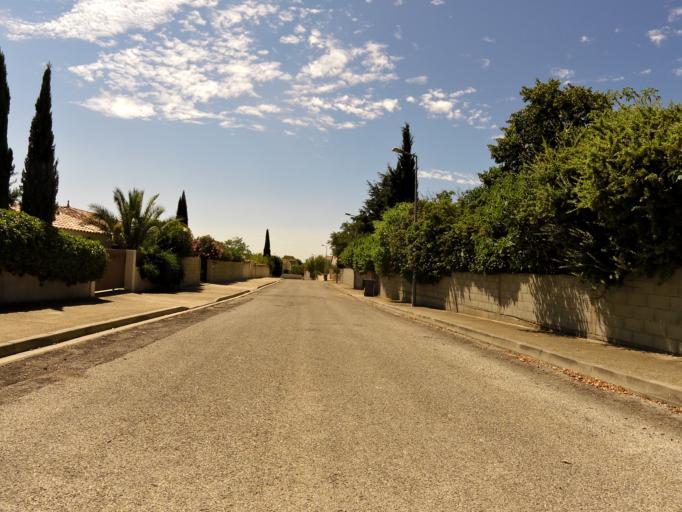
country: FR
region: Languedoc-Roussillon
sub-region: Departement du Gard
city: Vergeze
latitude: 43.7439
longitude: 4.2285
